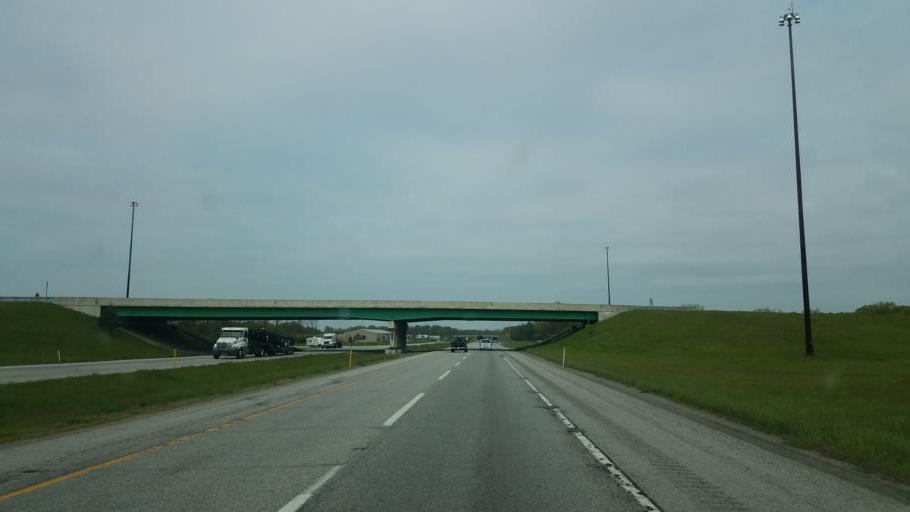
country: US
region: Indiana
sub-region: Elkhart County
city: Bristol
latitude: 41.7353
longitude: -85.7889
